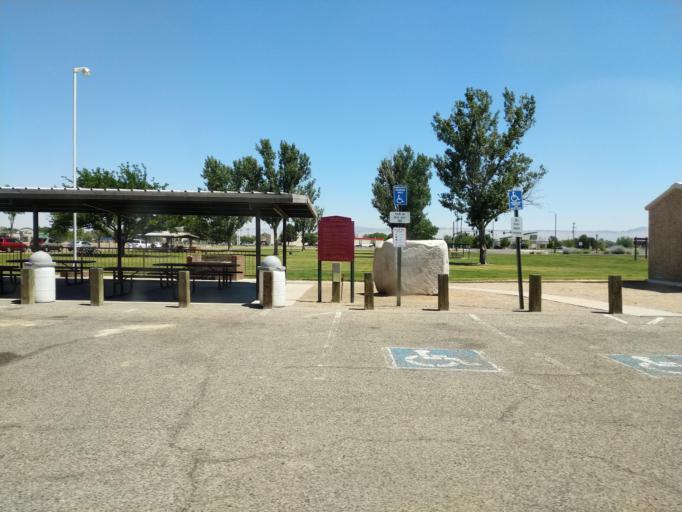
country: US
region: Colorado
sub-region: Mesa County
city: Orchard Mesa
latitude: 39.0371
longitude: -108.5399
